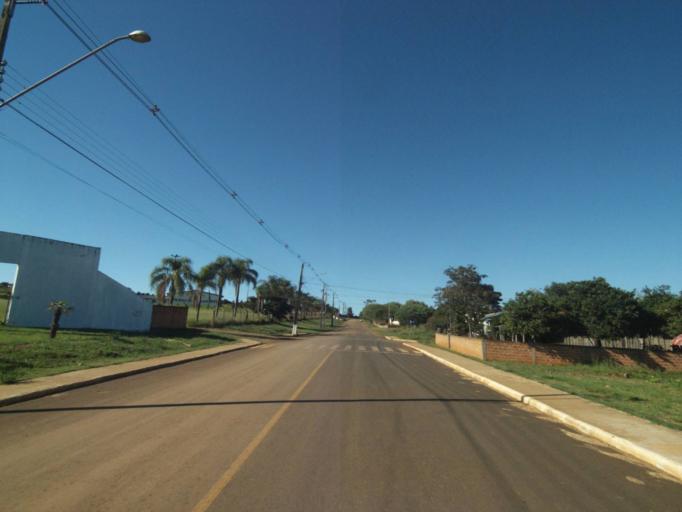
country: BR
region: Parana
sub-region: Pinhao
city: Pinhao
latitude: -25.8432
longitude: -52.0306
